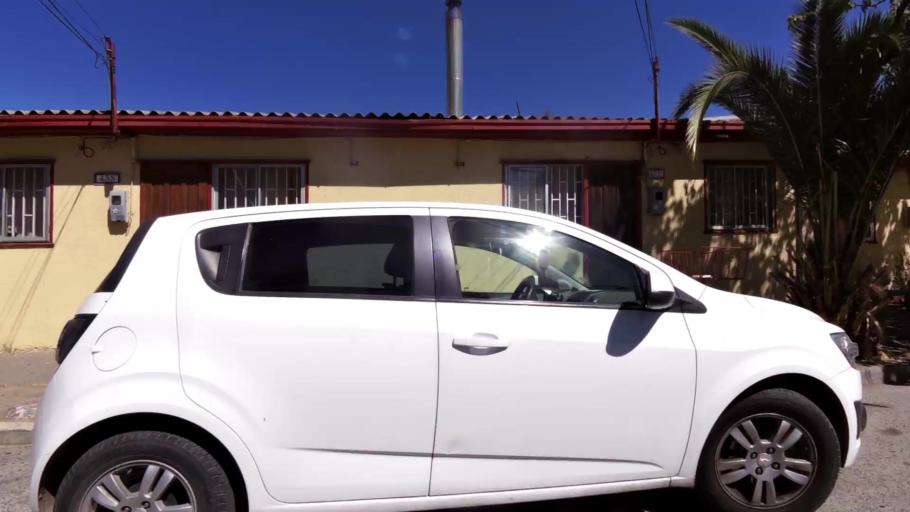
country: CL
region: O'Higgins
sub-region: Provincia de Cachapoal
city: Rancagua
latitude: -34.1722
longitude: -70.7304
